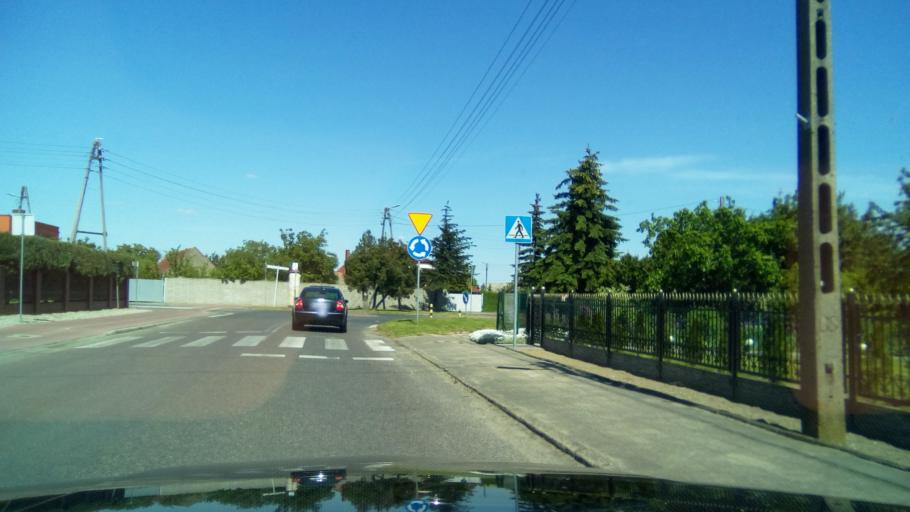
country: PL
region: Greater Poland Voivodeship
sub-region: Powiat gnieznienski
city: Niechanowo
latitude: 52.4647
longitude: 17.6765
